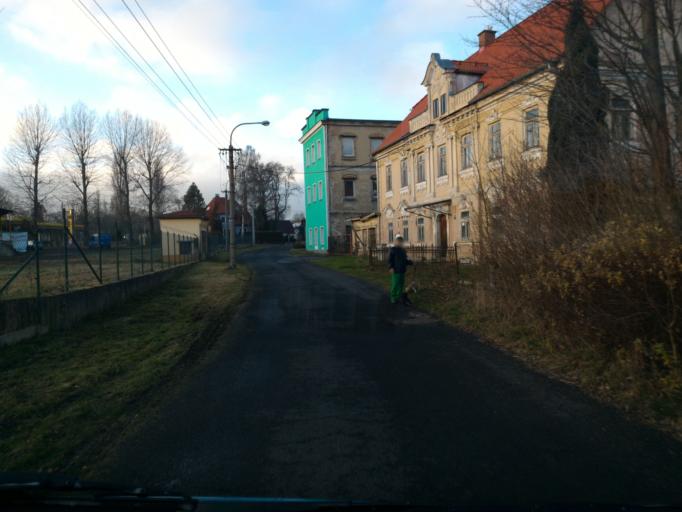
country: CZ
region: Ustecky
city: Varnsdorf
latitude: 50.9176
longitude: 14.6086
